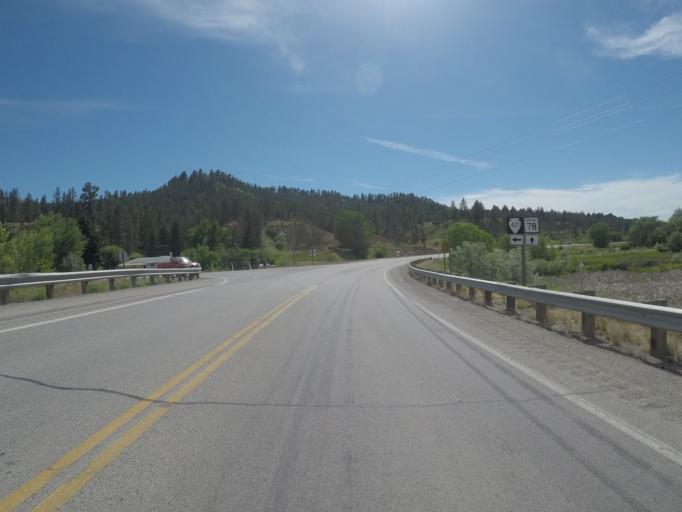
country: US
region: Montana
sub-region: Stillwater County
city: Columbus
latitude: 45.6272
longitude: -109.2572
